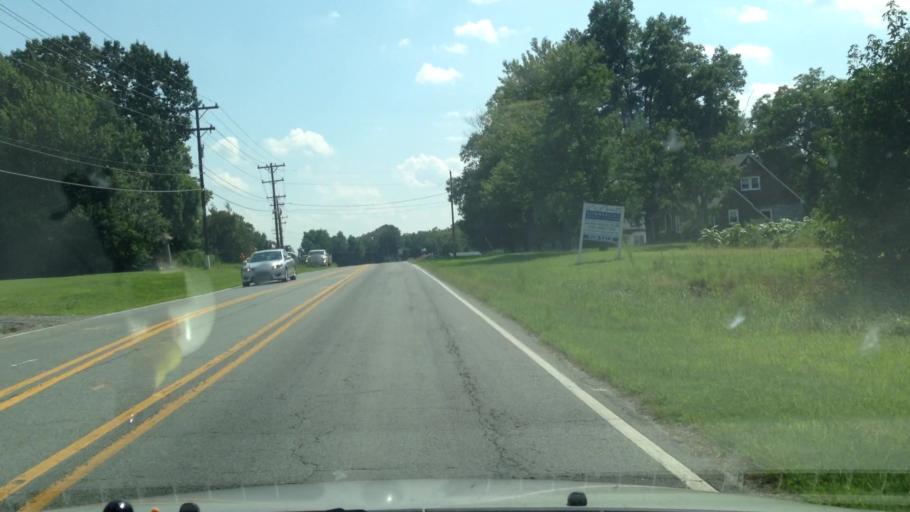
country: US
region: North Carolina
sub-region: Forsyth County
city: Kernersville
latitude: 36.1378
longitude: -80.0518
